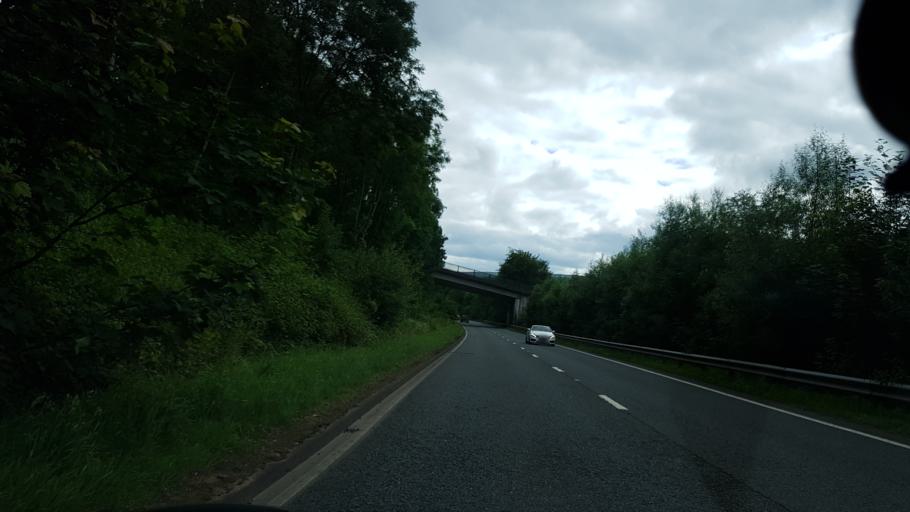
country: GB
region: Wales
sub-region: Monmouthshire
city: Abergavenny
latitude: 51.8250
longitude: -3.0055
